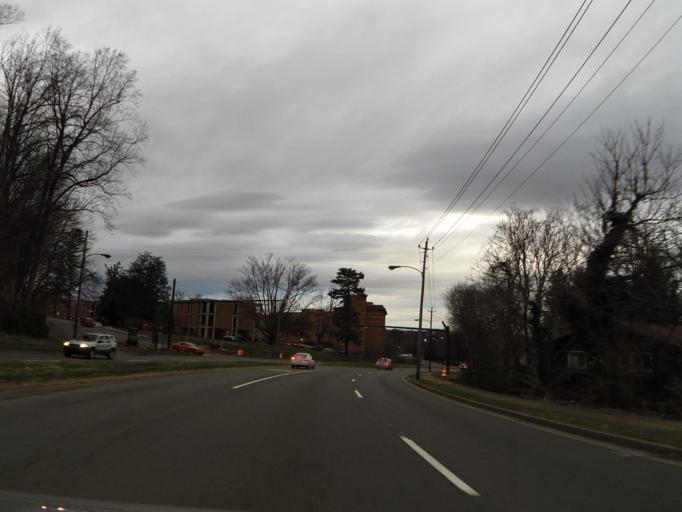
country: US
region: Tennessee
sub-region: Washington County
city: Johnson City
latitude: 36.3039
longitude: -82.3613
